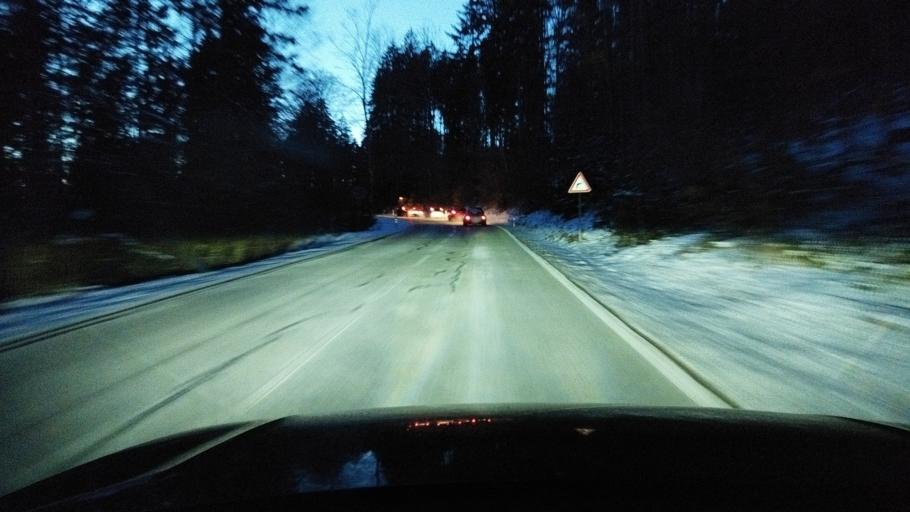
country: DE
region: Baden-Wuerttemberg
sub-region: Regierungsbezirk Stuttgart
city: Mainhardt
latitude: 49.0596
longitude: 9.6134
